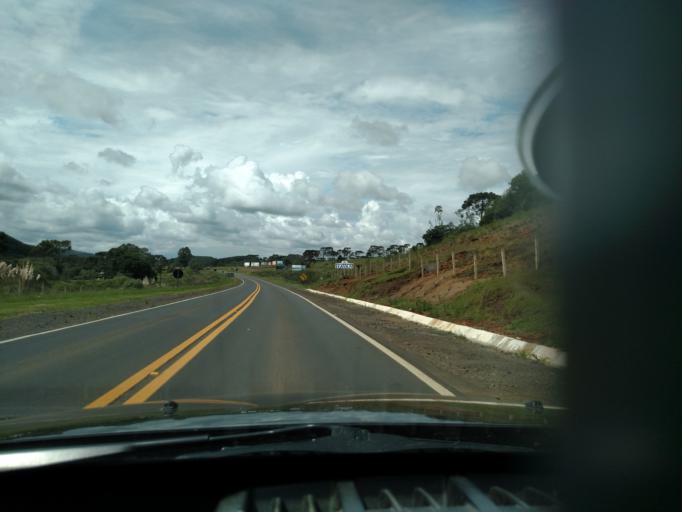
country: BR
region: Santa Catarina
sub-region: Lages
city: Lages
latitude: -27.9549
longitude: -50.4823
